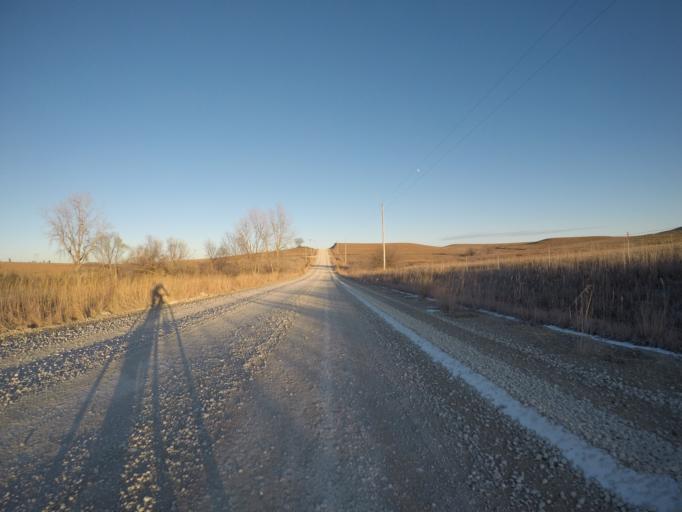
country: US
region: Kansas
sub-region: Pottawatomie County
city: Westmoreland
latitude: 39.3199
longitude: -96.5220
